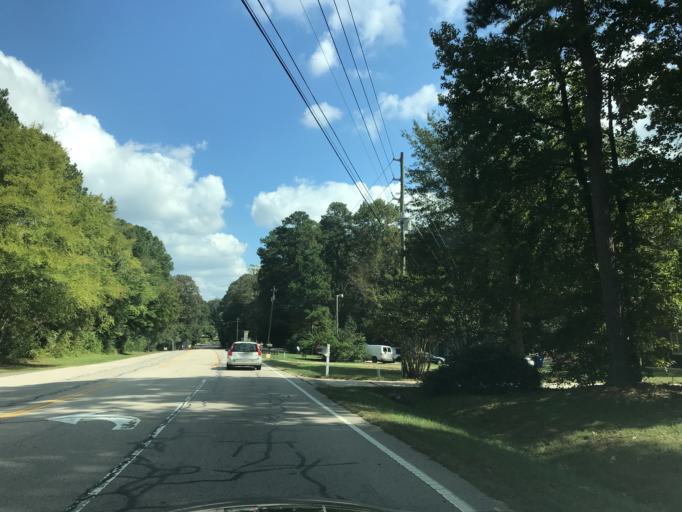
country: US
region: North Carolina
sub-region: Wake County
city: Rolesville
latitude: 35.8712
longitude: -78.5559
